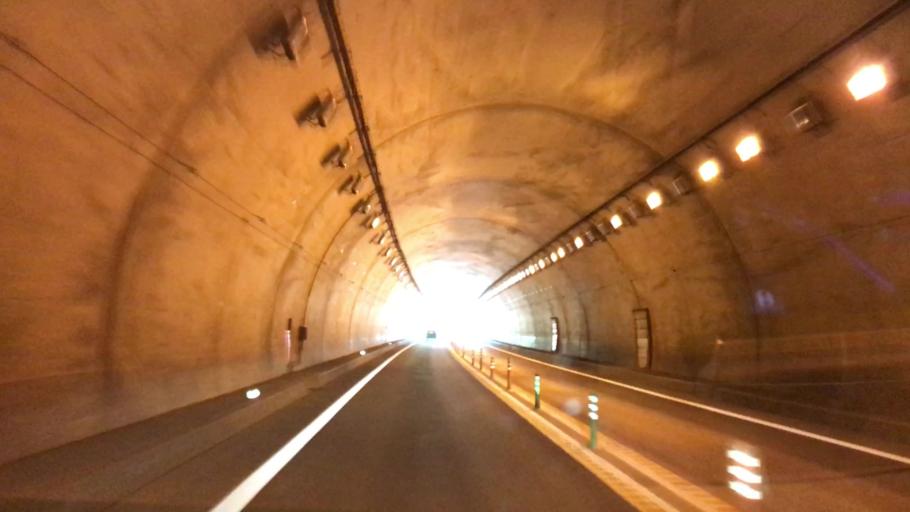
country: JP
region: Hokkaido
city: Chitose
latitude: 42.9074
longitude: 142.0108
